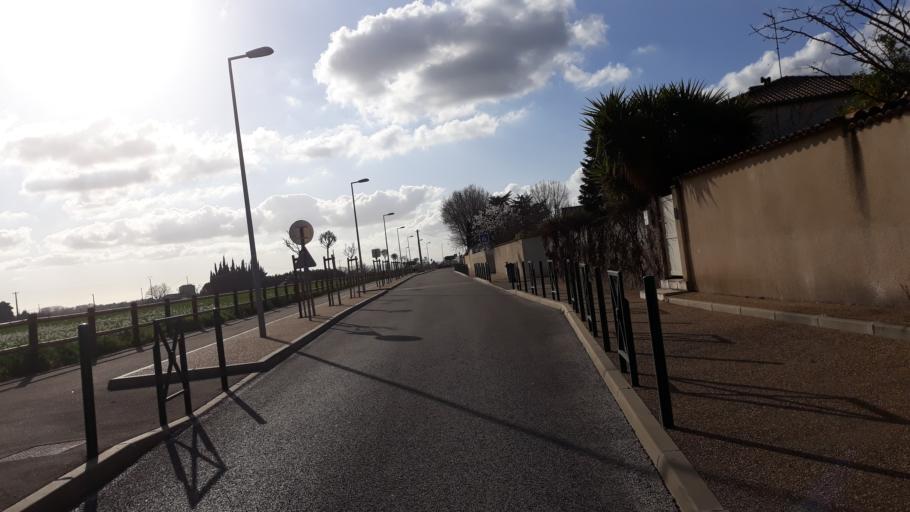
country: FR
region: Languedoc-Roussillon
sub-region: Departement du Gard
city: Aimargues
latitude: 43.6904
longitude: 4.2031
